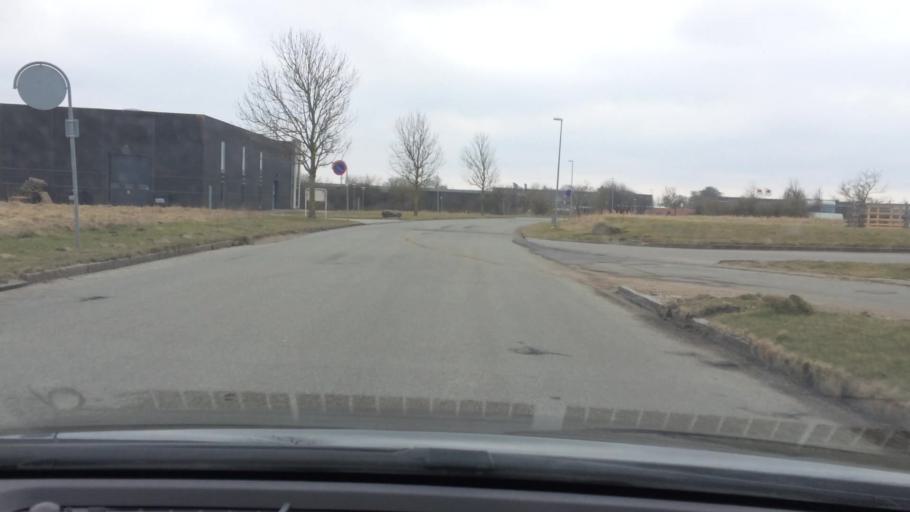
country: DK
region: South Denmark
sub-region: Vejle Kommune
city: Vejle
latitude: 55.7341
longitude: 9.5680
